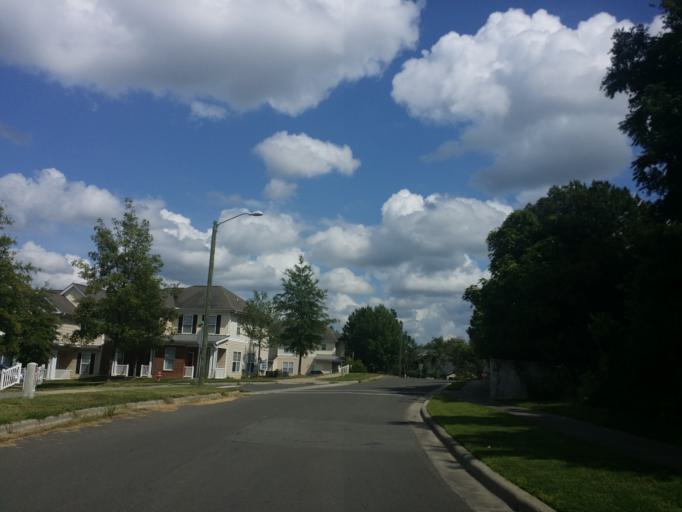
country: US
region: North Carolina
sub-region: Durham County
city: Durham
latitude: 35.9859
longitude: -78.8916
